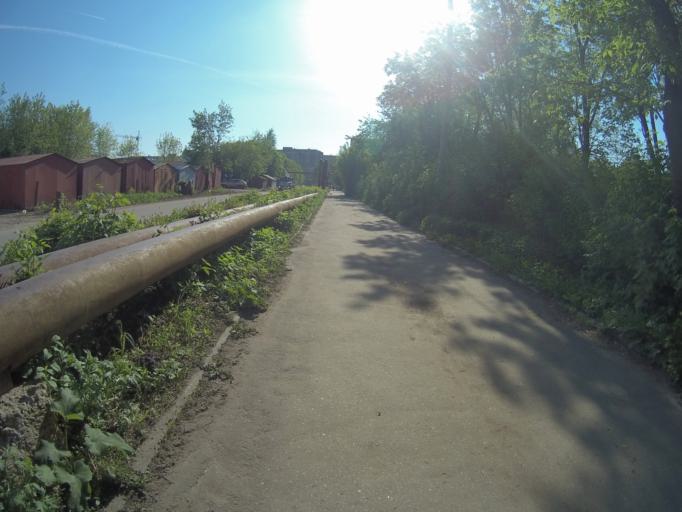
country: RU
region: Vladimir
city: Bogolyubovo
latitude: 56.1723
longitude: 40.4809
